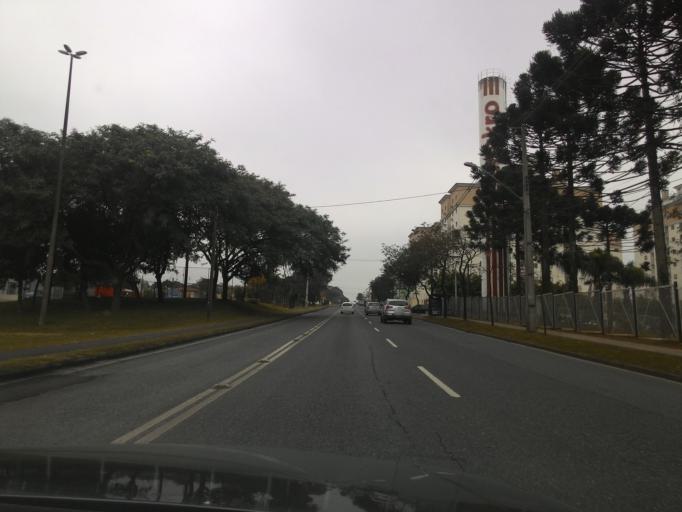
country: BR
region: Parana
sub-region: Curitiba
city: Curitiba
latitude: -25.4727
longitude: -49.2661
